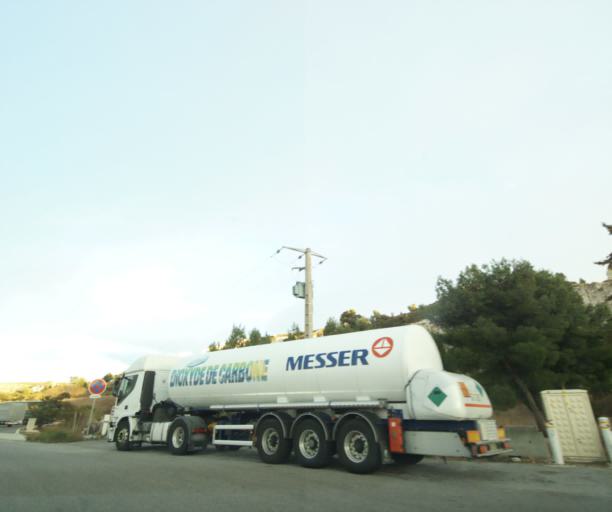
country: FR
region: Provence-Alpes-Cote d'Azur
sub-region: Departement des Bouches-du-Rhone
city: Le Rove
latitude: 43.3905
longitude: 5.2590
